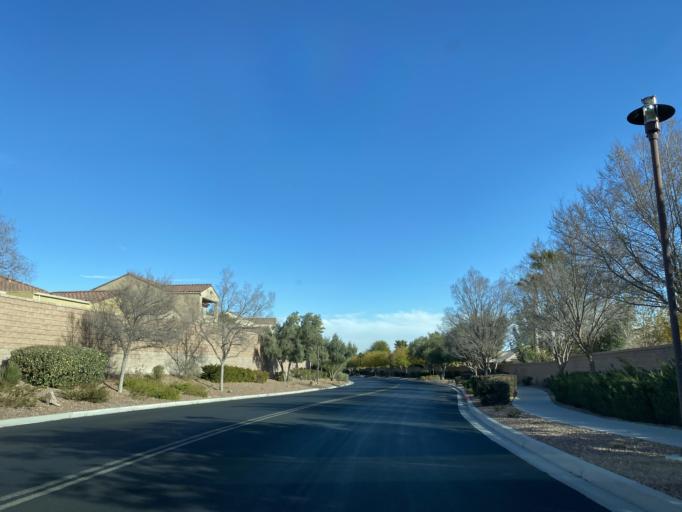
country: US
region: Nevada
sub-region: Clark County
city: North Las Vegas
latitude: 36.3178
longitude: -115.2560
